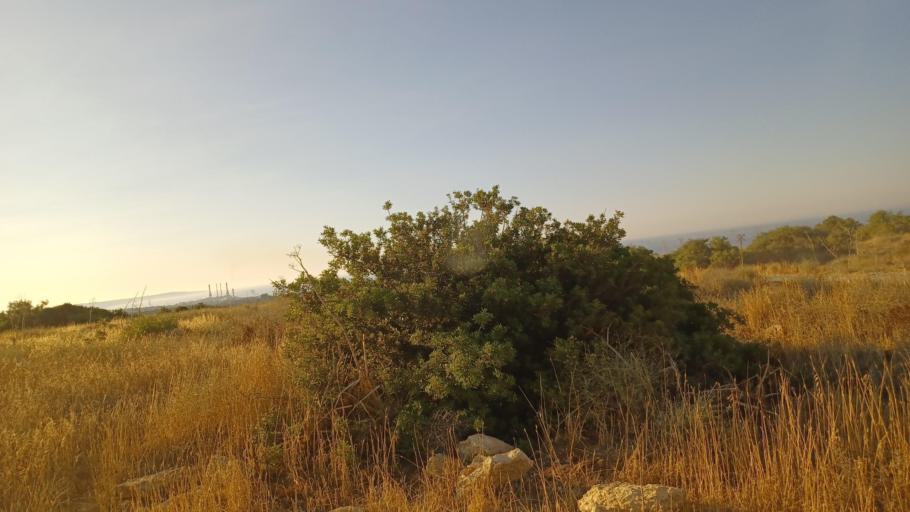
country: CY
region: Larnaka
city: Pyla
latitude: 34.9945
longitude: 33.7063
